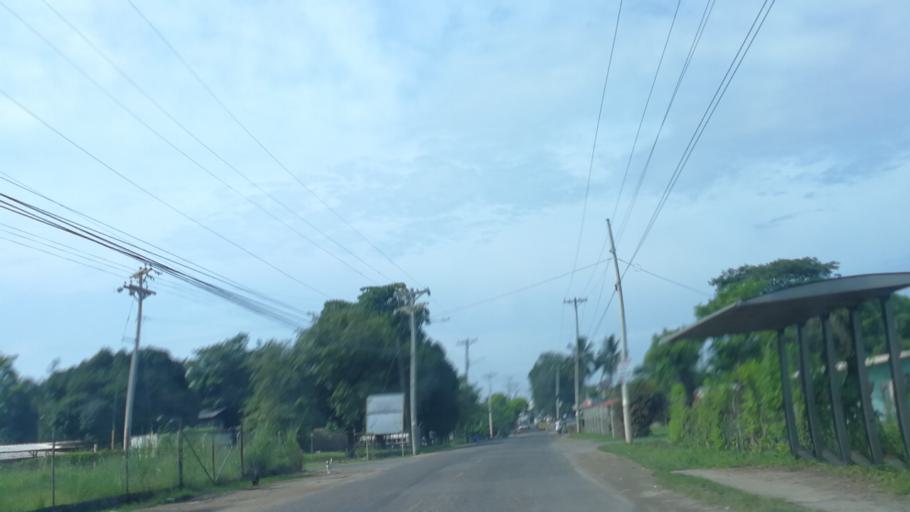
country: PA
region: Panama
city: Pacora
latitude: 9.0862
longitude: -79.2872
